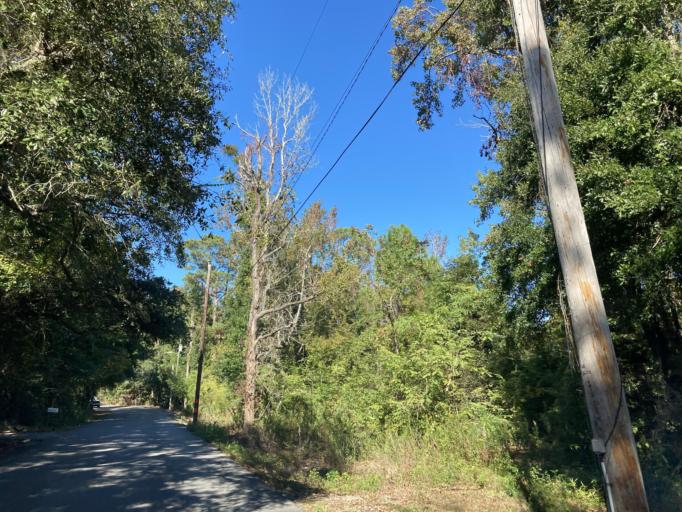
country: US
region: Mississippi
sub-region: Jackson County
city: Ocean Springs
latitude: 30.4010
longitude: -88.8164
